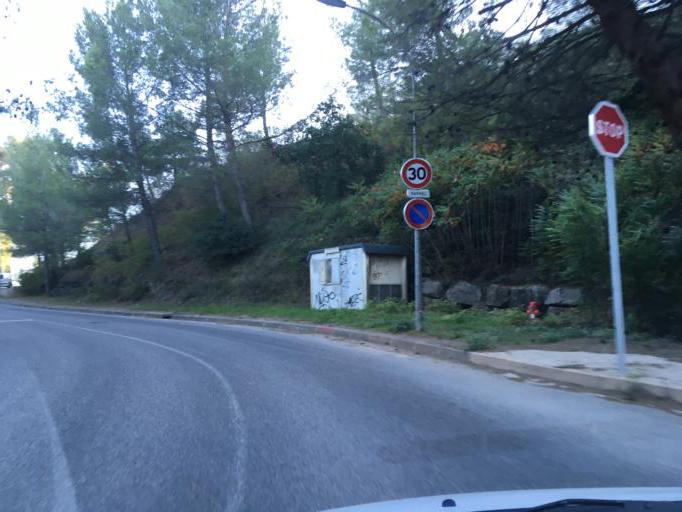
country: FR
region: Provence-Alpes-Cote d'Azur
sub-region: Departement des Bouches-du-Rhone
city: Ceyreste
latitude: 43.2091
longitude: 5.6036
